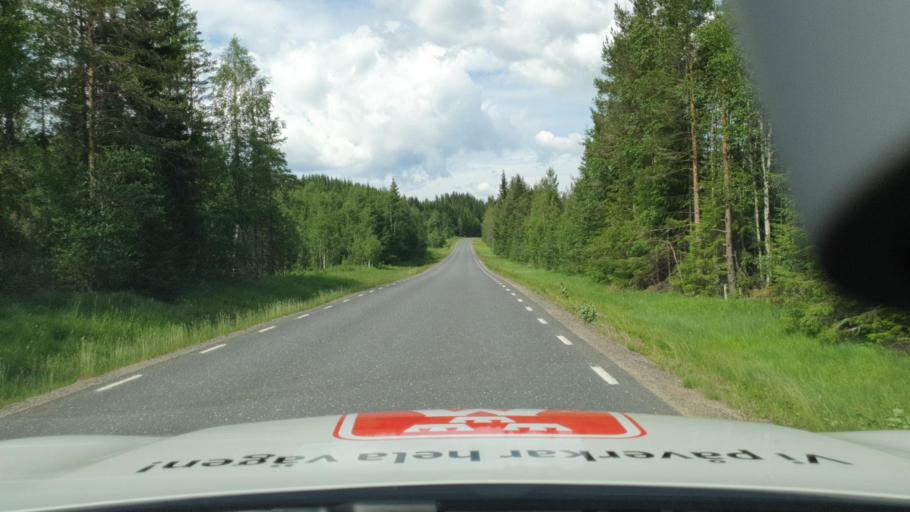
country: SE
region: Vaermland
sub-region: Torsby Kommun
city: Torsby
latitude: 60.5931
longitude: 12.7337
